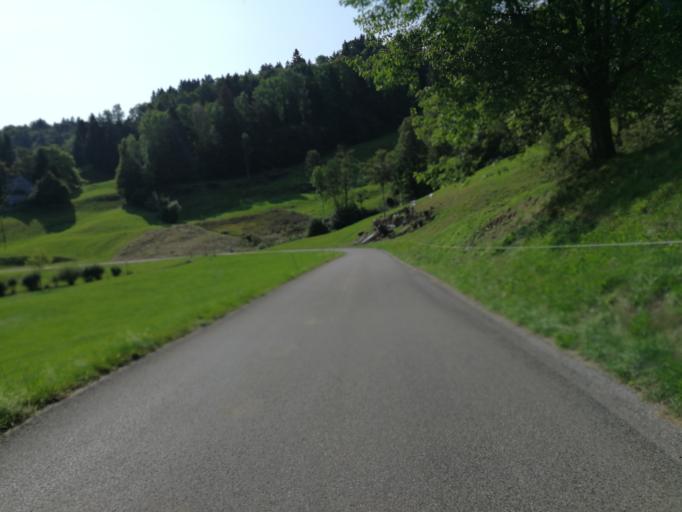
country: CH
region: Saint Gallen
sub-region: Wahlkreis Toggenburg
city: Krummenau
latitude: 47.2471
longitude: 9.1505
